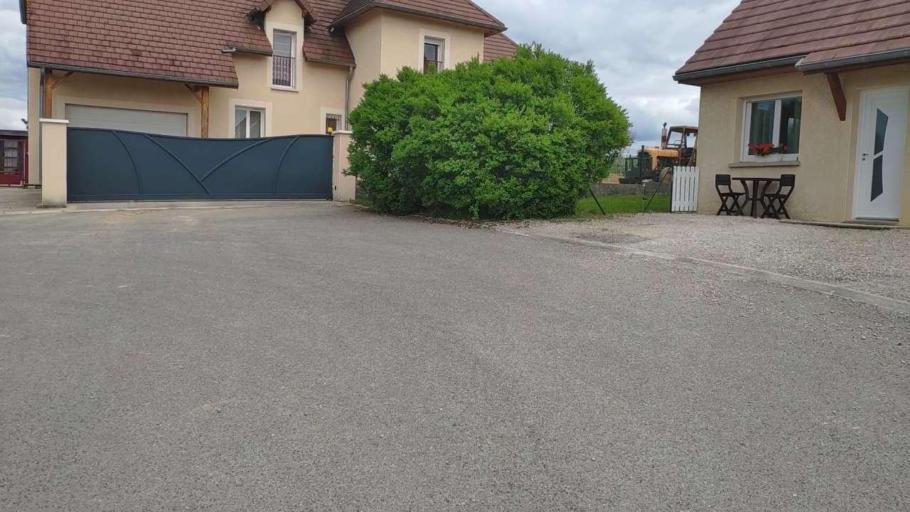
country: FR
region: Franche-Comte
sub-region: Departement du Jura
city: Bletterans
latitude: 46.7391
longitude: 5.5054
